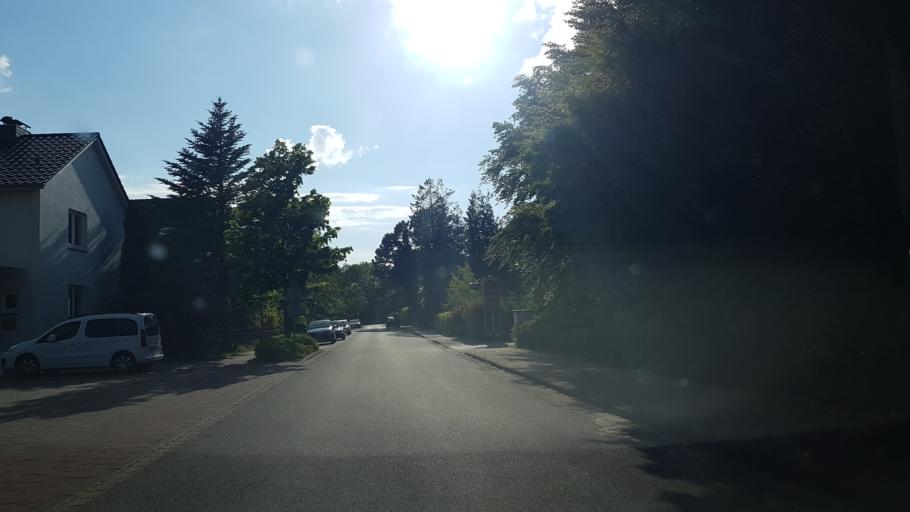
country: DE
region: Lower Saxony
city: Langen
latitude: 53.6031
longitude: 8.5893
